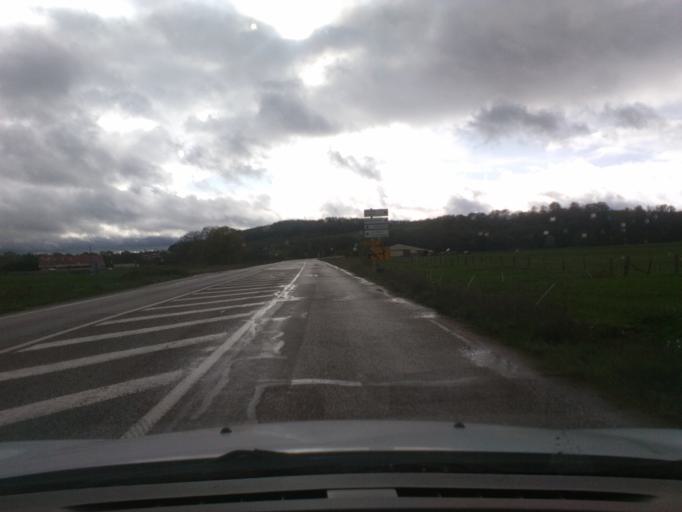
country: FR
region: Lorraine
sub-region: Departement des Vosges
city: Charmes
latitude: 48.3779
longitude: 6.2703
